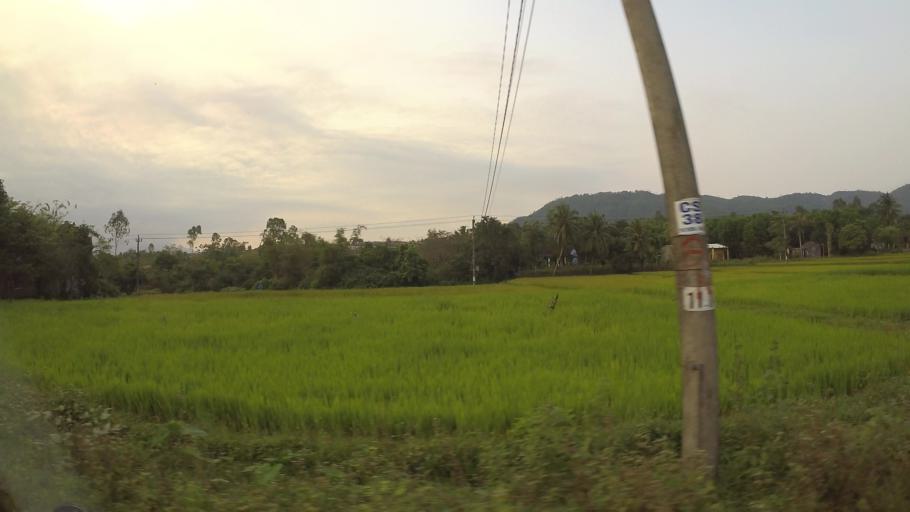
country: VN
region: Da Nang
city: Lien Chieu
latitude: 16.0533
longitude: 108.1128
